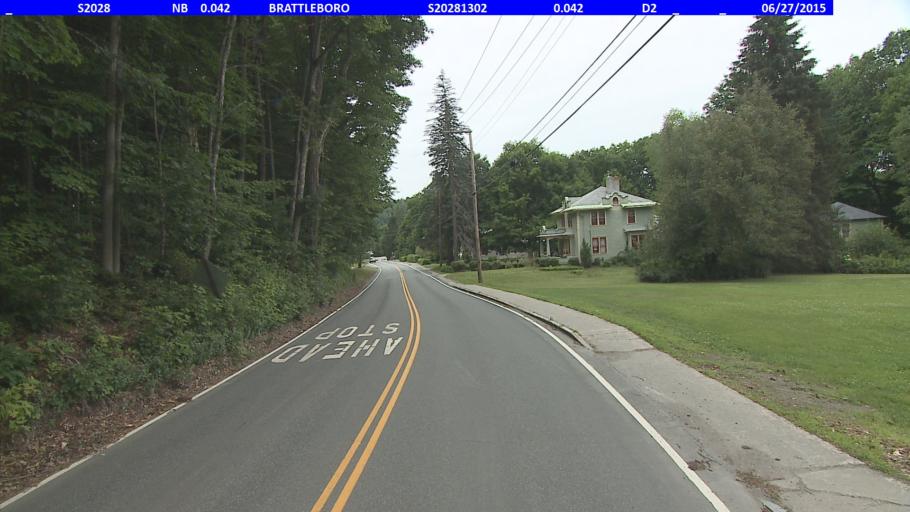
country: US
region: Vermont
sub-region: Windham County
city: West Brattleboro
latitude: 42.8454
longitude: -72.5829
